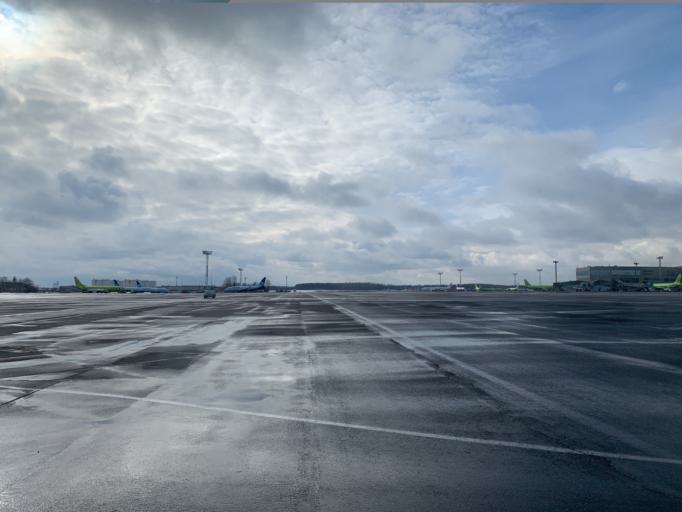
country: RU
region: Moskovskaya
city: Yakovlevskoye
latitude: 55.4121
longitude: 37.9080
